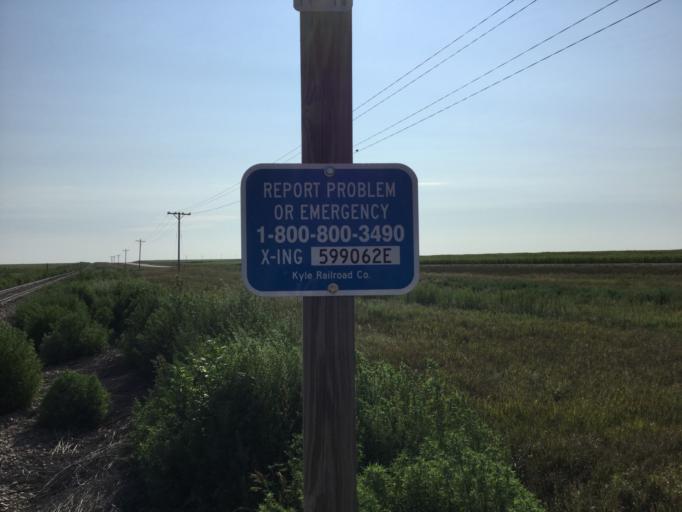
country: US
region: Kansas
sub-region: Sheridan County
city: Hoxie
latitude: 39.4798
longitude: -100.7205
